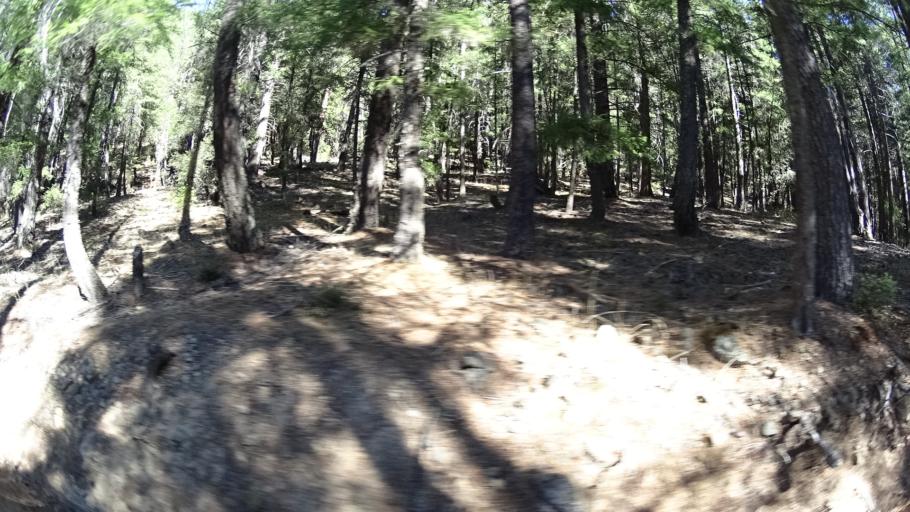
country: US
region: California
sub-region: Siskiyou County
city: Happy Camp
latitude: 41.2983
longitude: -123.1191
